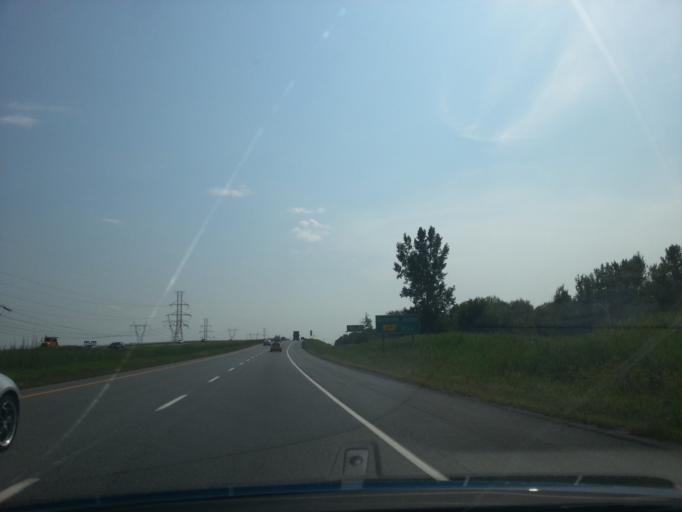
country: CA
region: Quebec
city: Saint-Bruno-de-Montarville
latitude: 45.4722
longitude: -73.3906
